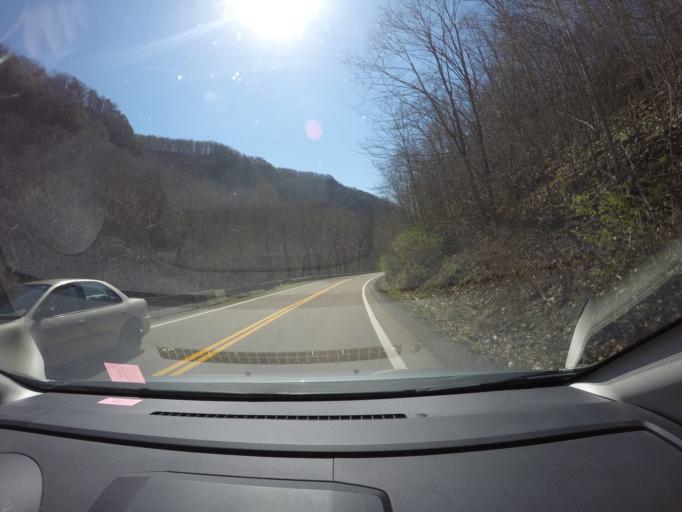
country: US
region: Tennessee
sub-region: Hamilton County
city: Signal Mountain
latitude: 35.1410
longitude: -85.3863
